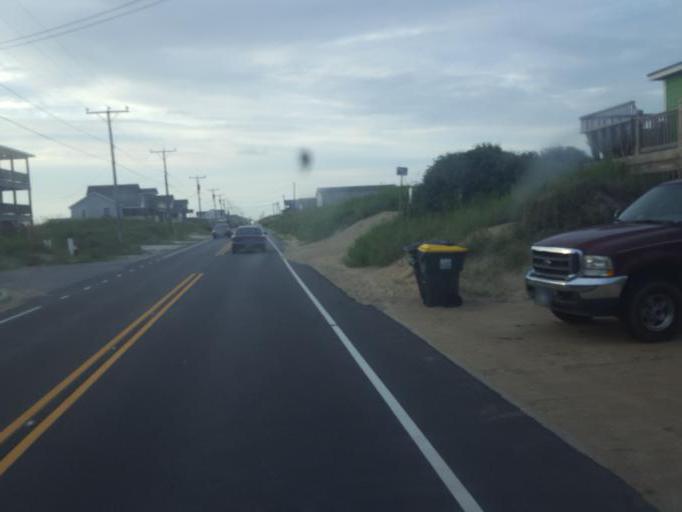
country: US
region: North Carolina
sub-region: Dare County
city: Kill Devil Hills
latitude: 36.0538
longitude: -75.6817
